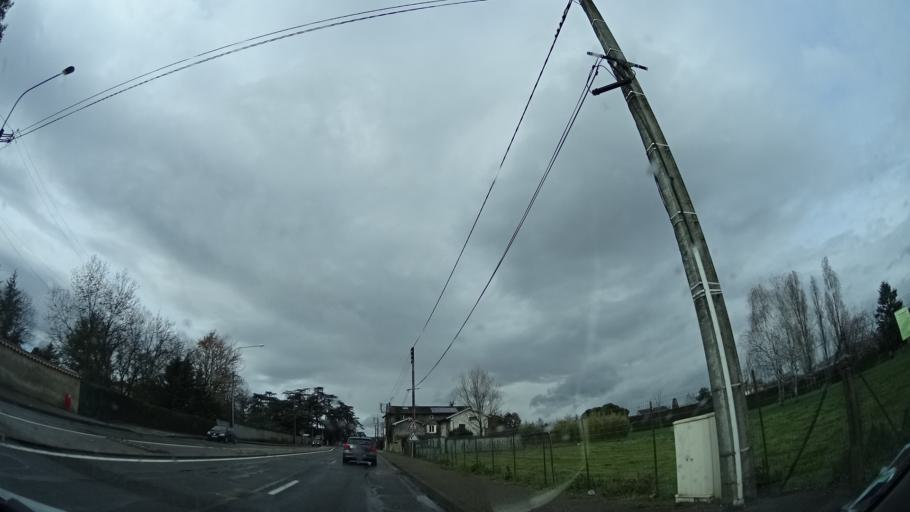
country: FR
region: Rhone-Alpes
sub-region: Departement du Rhone
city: Charbonnieres-les-Bains
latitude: 45.7884
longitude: 4.7458
